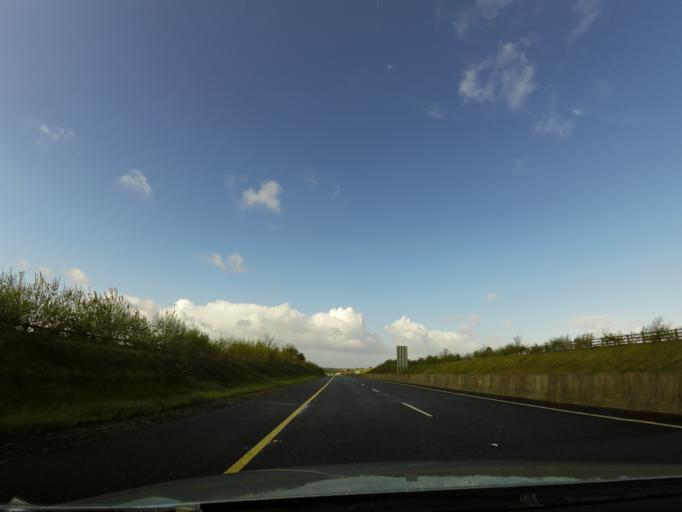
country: IE
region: Munster
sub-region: North Tipperary
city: Newport
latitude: 52.7491
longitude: -8.4276
